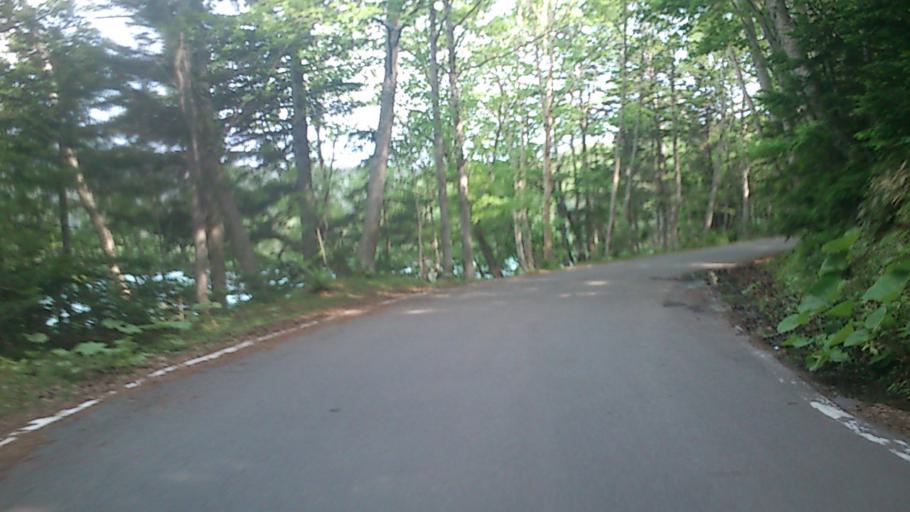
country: JP
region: Hokkaido
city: Kitami
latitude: 43.3847
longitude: 143.9659
